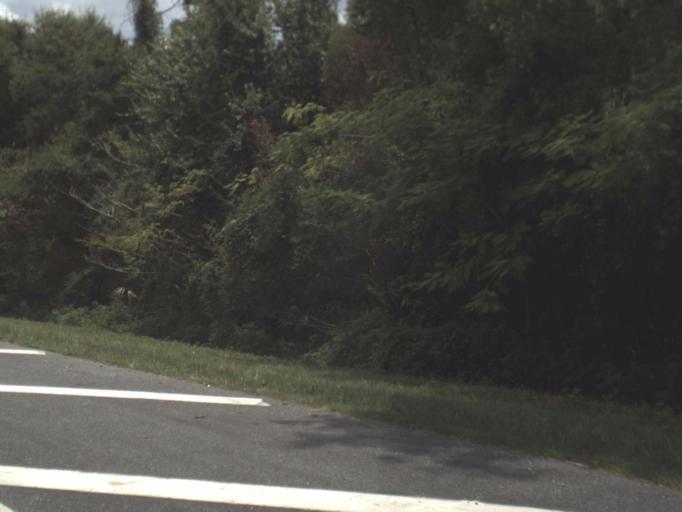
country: US
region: Florida
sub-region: Taylor County
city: Perry
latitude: 30.0873
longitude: -83.5303
